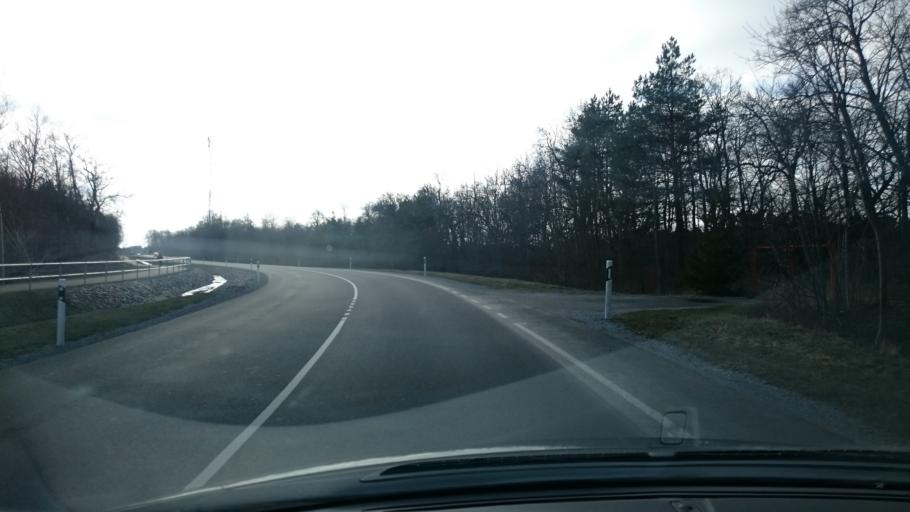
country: EE
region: Harju
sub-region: Paldiski linn
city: Paldiski
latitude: 59.3841
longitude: 24.2354
